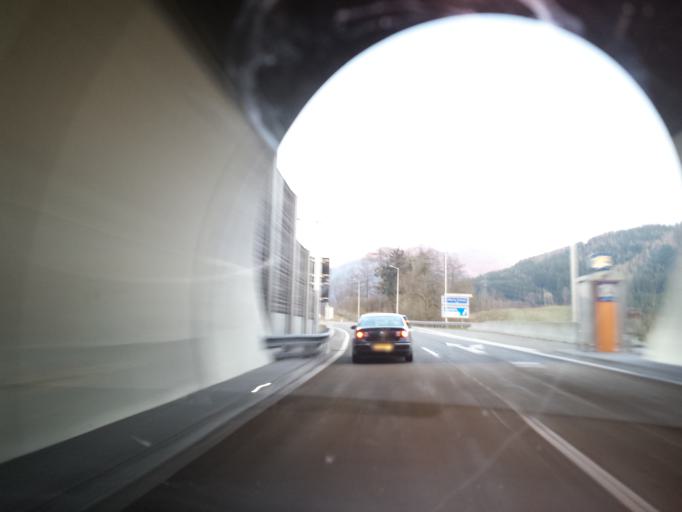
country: AT
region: Styria
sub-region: Politischer Bezirk Bruck-Muerzzuschlag
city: Spital am Semmering
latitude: 47.6120
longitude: 15.7416
